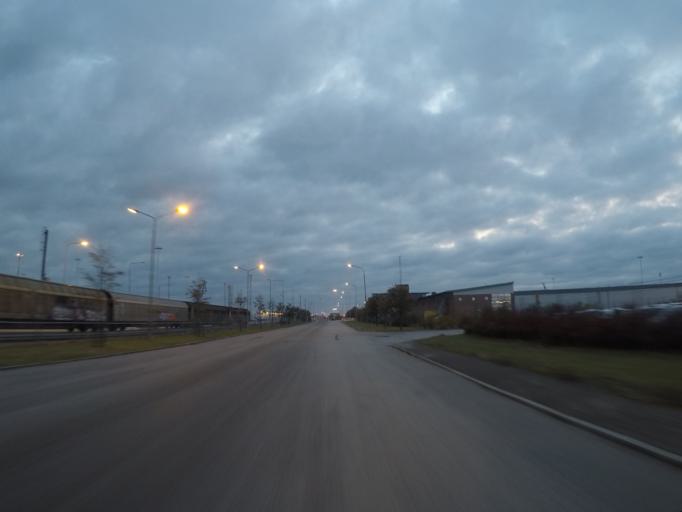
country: SE
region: Skane
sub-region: Malmo
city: Malmoe
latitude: 55.6206
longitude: 13.0083
